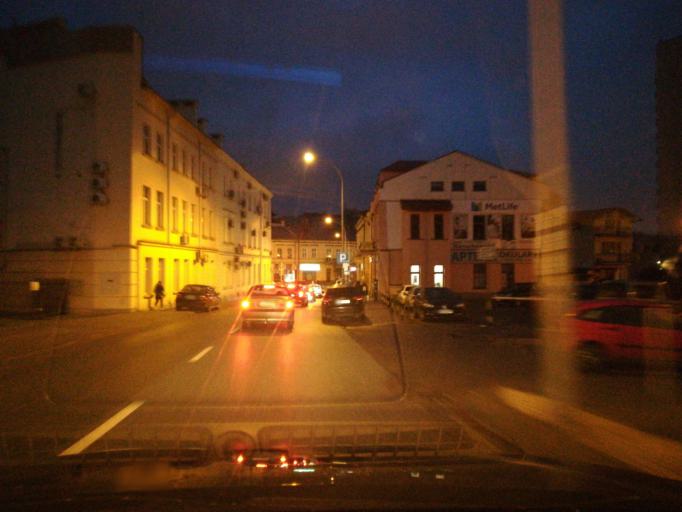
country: PL
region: Subcarpathian Voivodeship
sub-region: Rzeszow
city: Rzeszow
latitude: 50.0422
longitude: 22.0013
